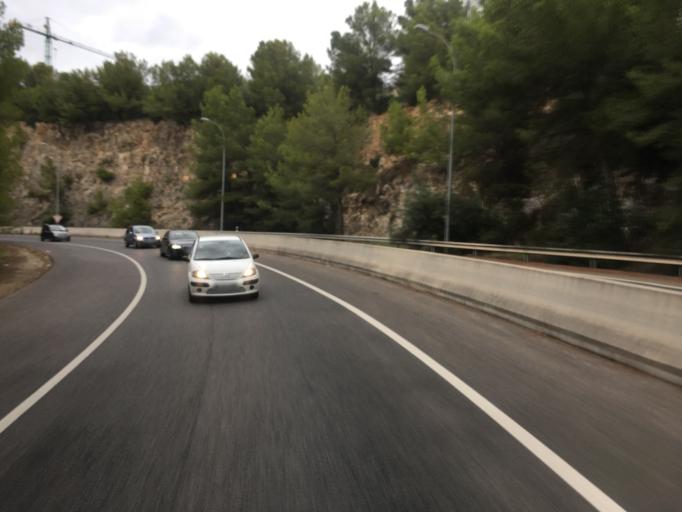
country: ES
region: Balearic Islands
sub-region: Illes Balears
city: Palma
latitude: 39.5534
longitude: 2.6167
